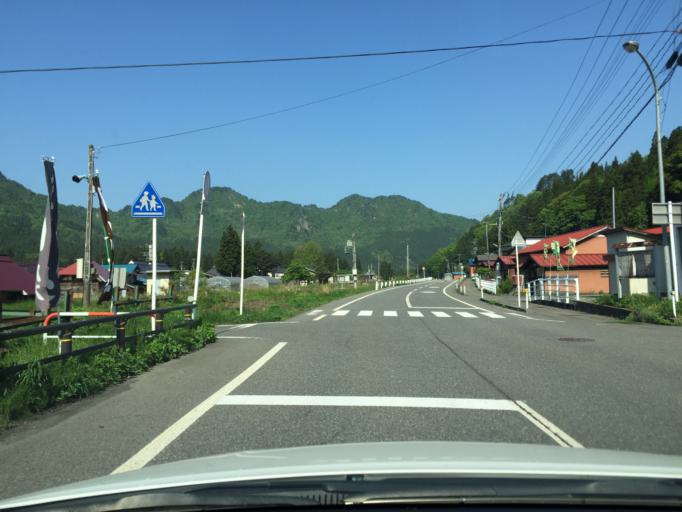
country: JP
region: Niigata
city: Shibata
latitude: 37.7053
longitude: 139.5377
